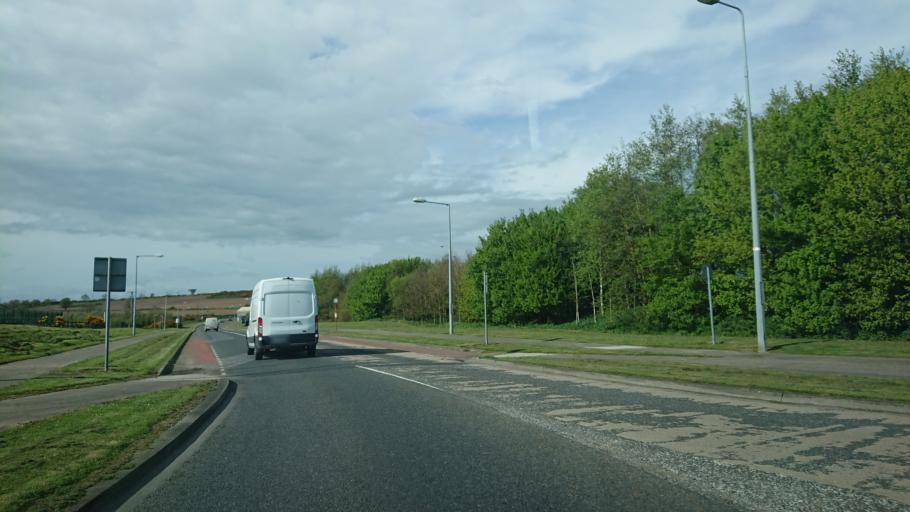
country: IE
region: Munster
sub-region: Waterford
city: Waterford
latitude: 52.2527
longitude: -7.1562
